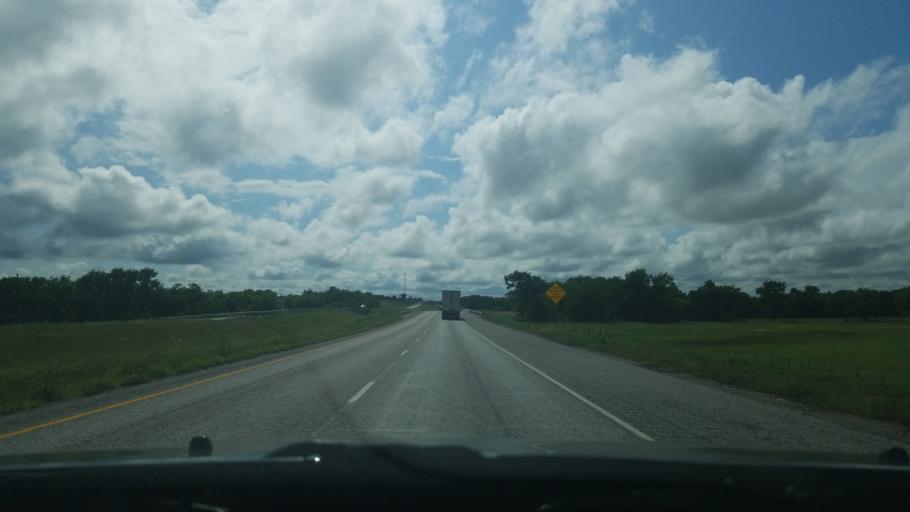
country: US
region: Texas
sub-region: Denton County
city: Krum
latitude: 33.2358
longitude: -97.2625
